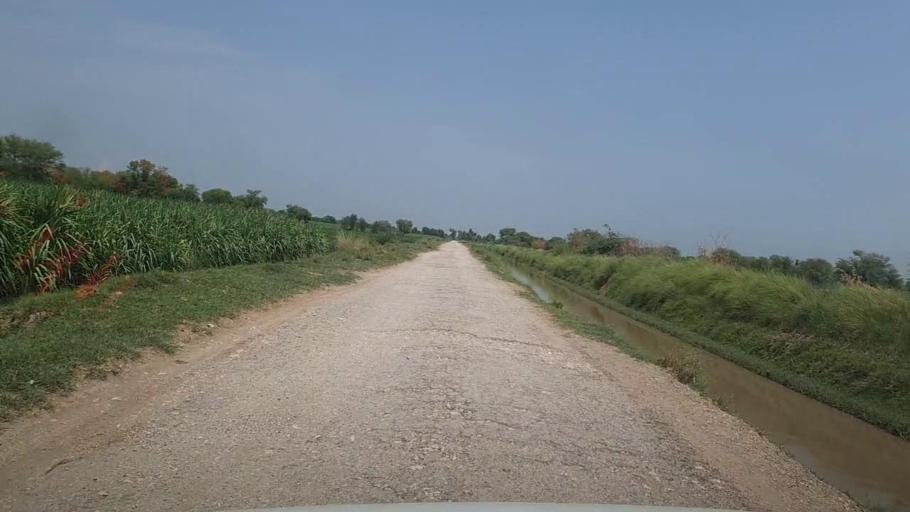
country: PK
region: Sindh
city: Karaundi
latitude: 26.8840
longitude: 68.3345
